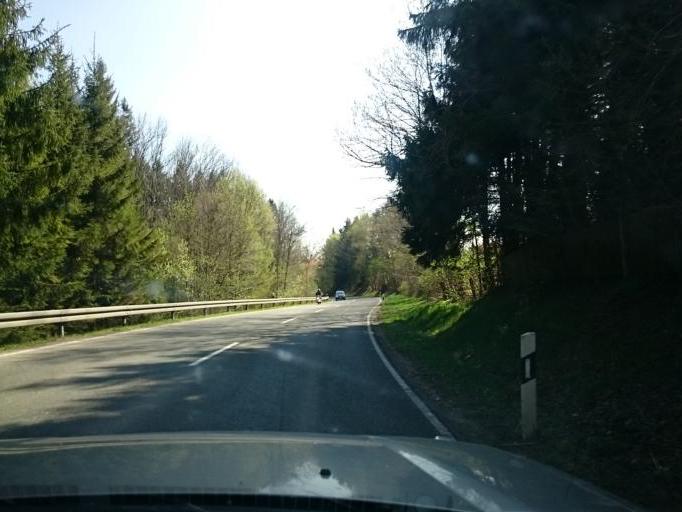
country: DE
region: Bavaria
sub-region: Upper Bavaria
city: Murnau am Staffelsee
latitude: 47.6727
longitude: 11.2157
